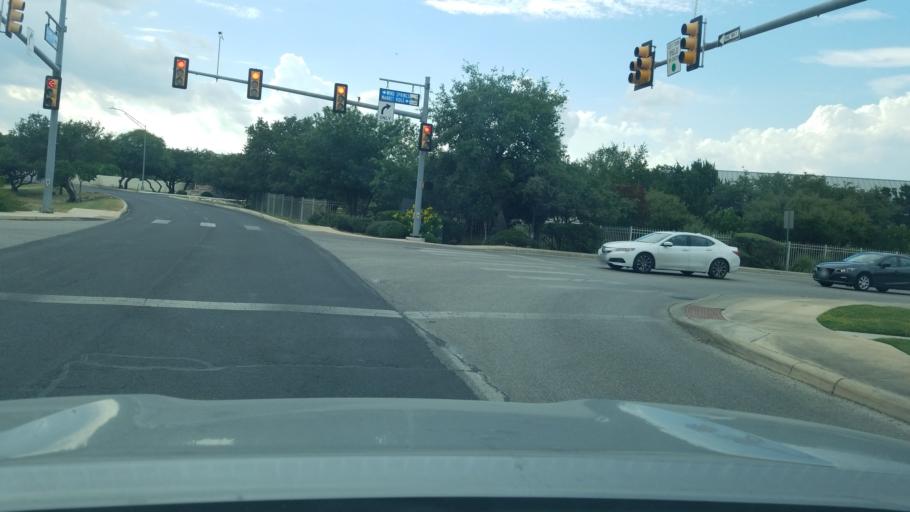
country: US
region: Texas
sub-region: Bexar County
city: Hollywood Park
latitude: 29.6387
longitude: -98.4587
